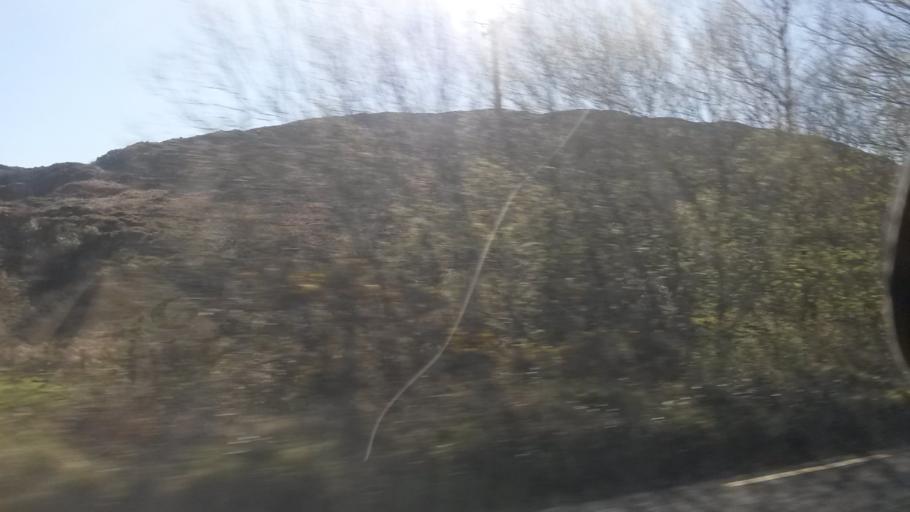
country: IE
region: Munster
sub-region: Ciarrai
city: Cill Airne
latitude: 51.9342
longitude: -9.3827
